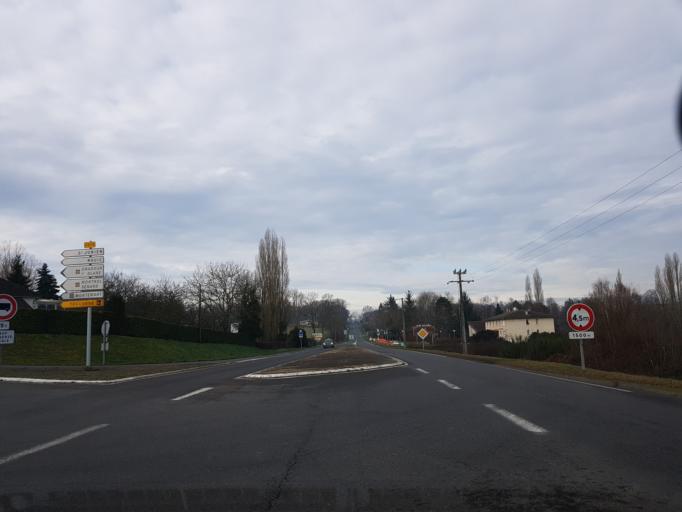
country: FR
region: Limousin
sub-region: Departement de la Haute-Vienne
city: Peyrat-de-Bellac
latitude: 46.1245
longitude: 1.0269
